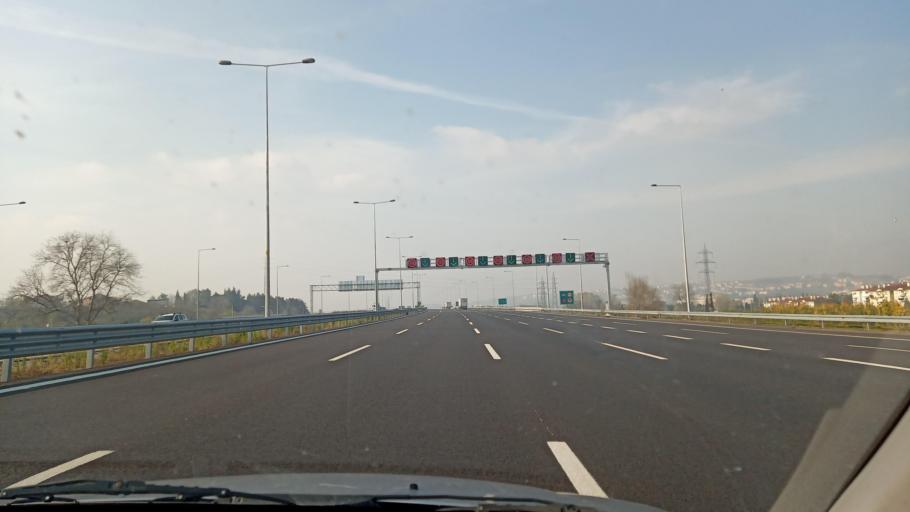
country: TR
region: Sakarya
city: Kazimpasa
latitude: 40.8438
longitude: 30.3377
